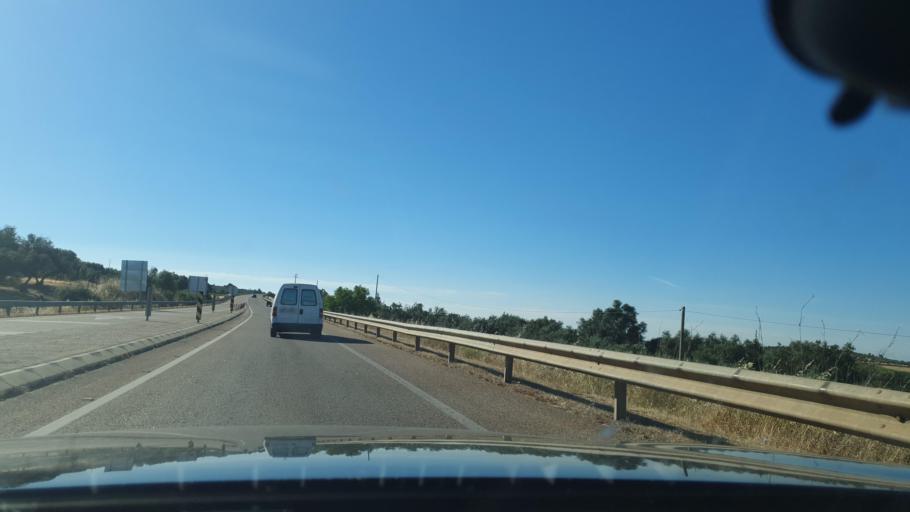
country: PT
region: Evora
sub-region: Vila Vicosa
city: Vila Vicosa
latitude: 38.7703
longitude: -7.4301
